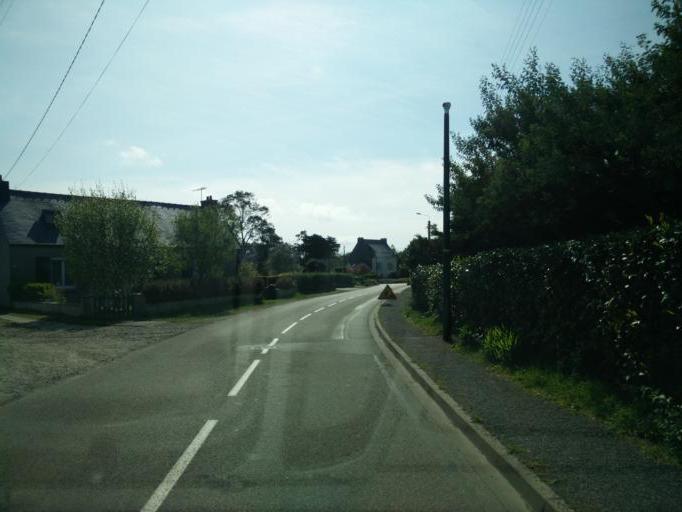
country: FR
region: Brittany
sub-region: Departement du Finistere
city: Crozon
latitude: 48.2431
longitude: -4.4796
